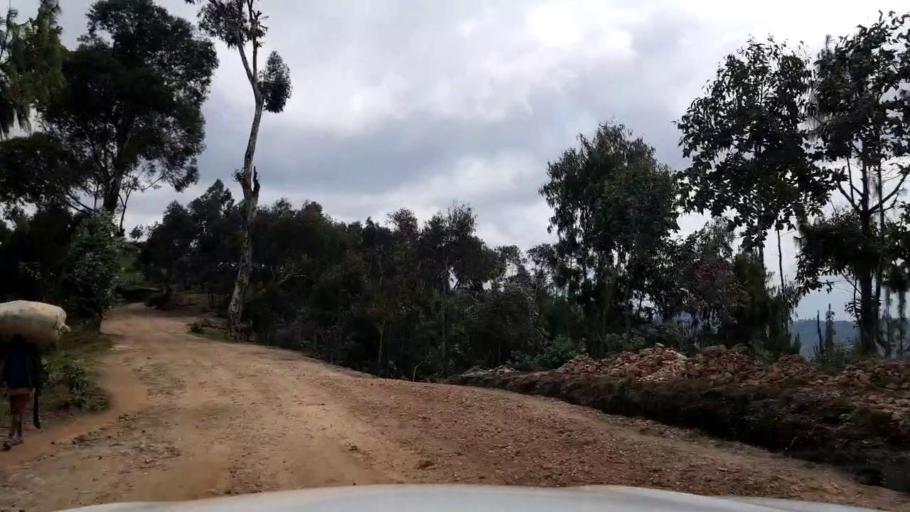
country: RW
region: Western Province
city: Kibuye
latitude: -1.9417
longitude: 29.4672
